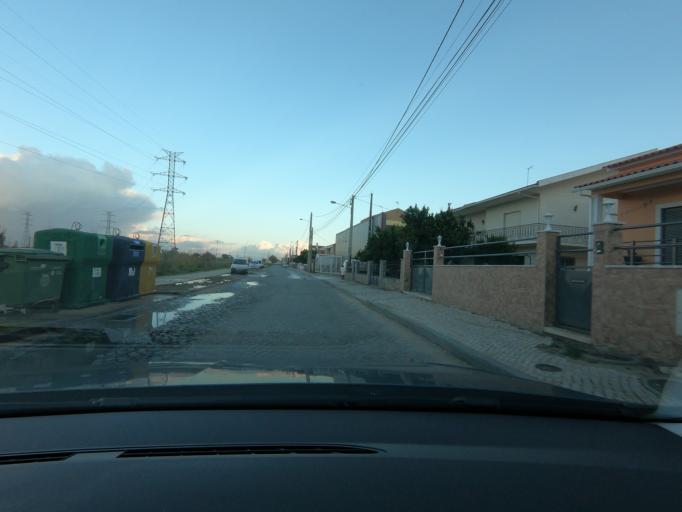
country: PT
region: Lisbon
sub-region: Vila Franca de Xira
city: Castanheira do Ribatejo
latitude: 39.0093
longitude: -8.9570
